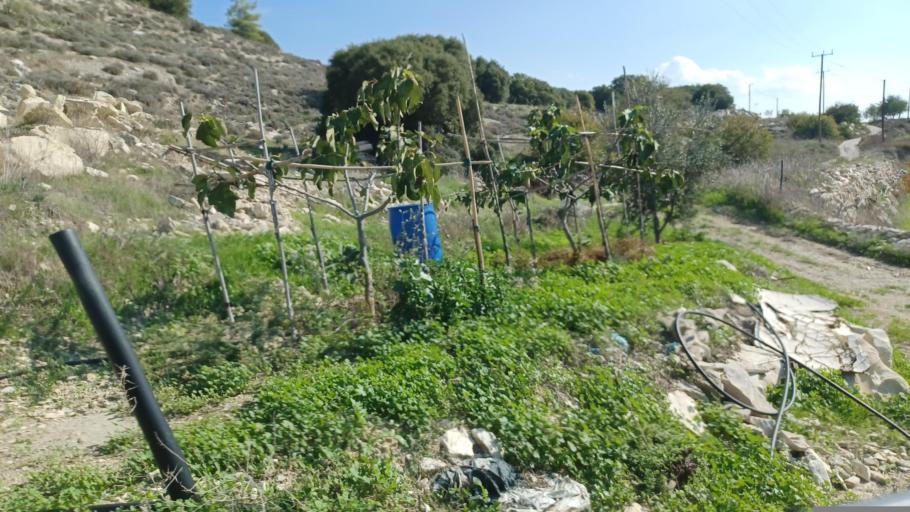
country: CY
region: Pafos
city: Mesogi
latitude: 34.8489
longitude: 32.5135
